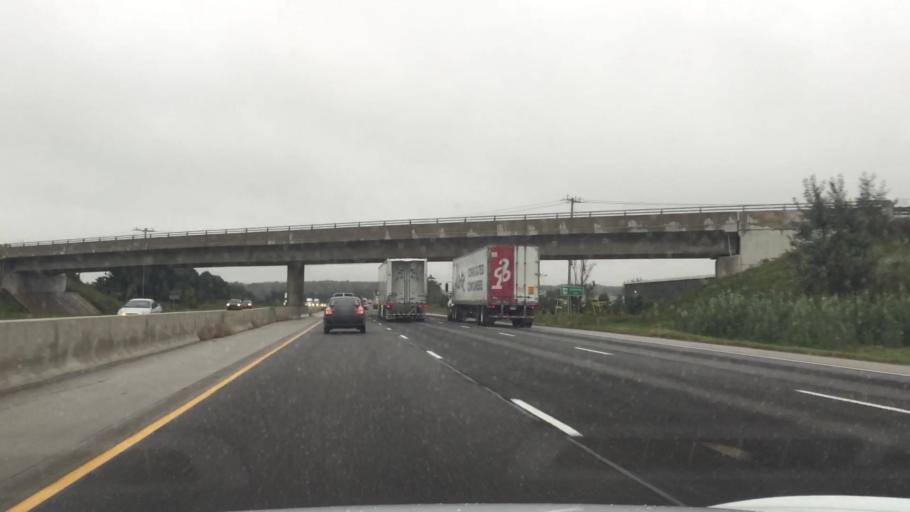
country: CA
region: Ontario
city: Kitchener
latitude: 43.3121
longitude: -80.4742
